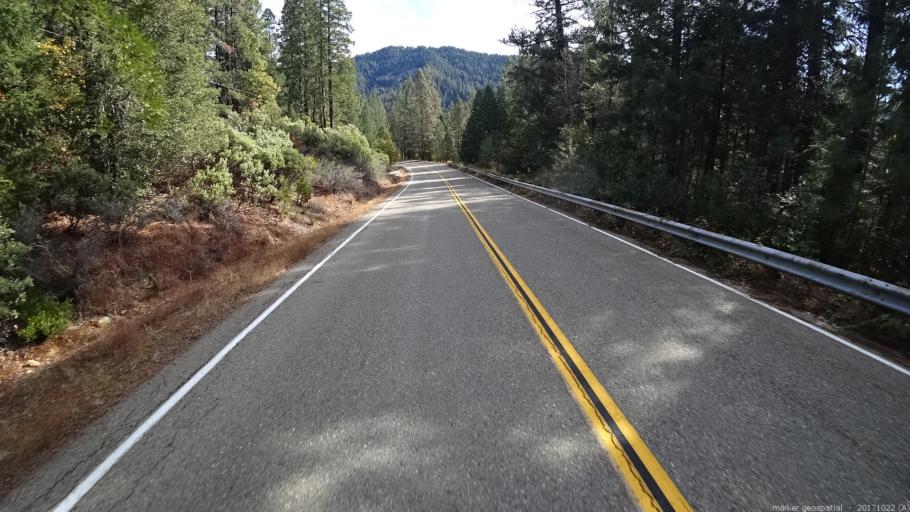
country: US
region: California
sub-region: Siskiyou County
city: Dunsmuir
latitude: 41.0656
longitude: -122.3656
